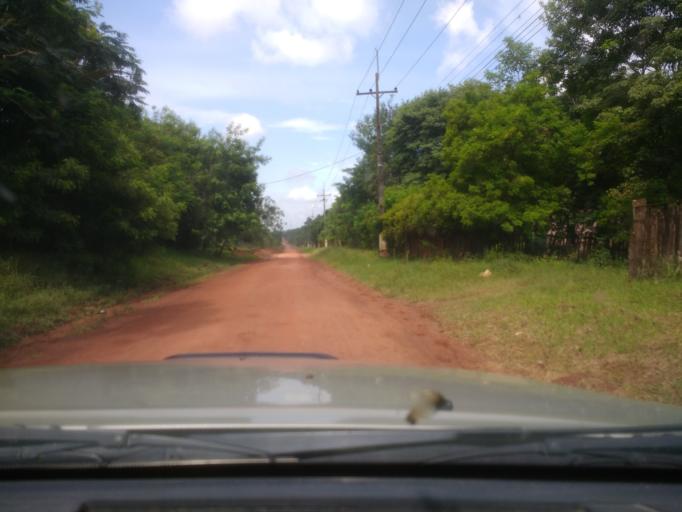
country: PY
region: San Pedro
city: Puerto Rosario
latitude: -24.4126
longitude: -57.1040
